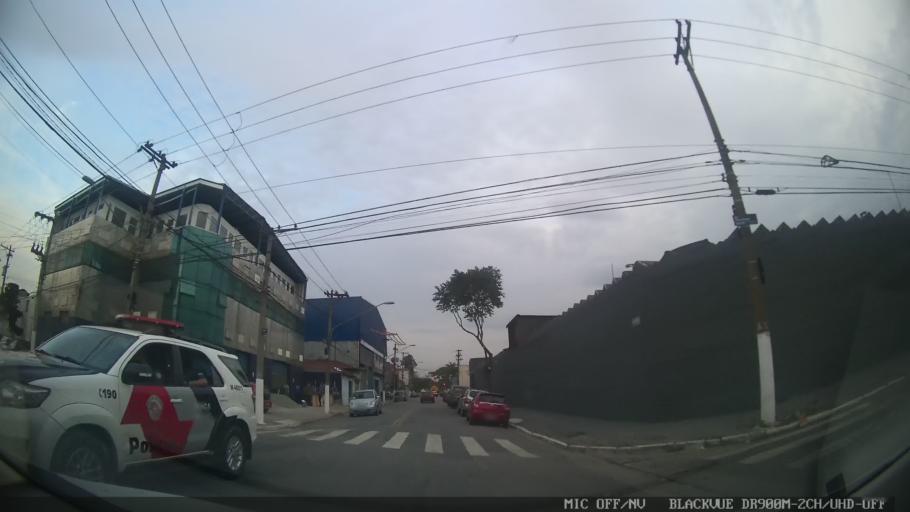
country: BR
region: Sao Paulo
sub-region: Sao Caetano Do Sul
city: Sao Caetano do Sul
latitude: -23.6004
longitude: -46.5877
